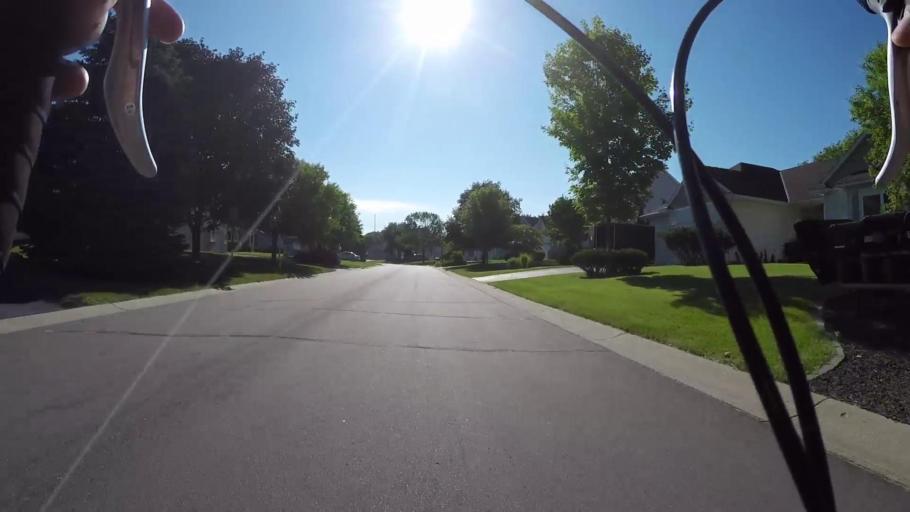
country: US
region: Minnesota
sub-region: Hennepin County
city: Eden Prairie
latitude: 44.8748
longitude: -93.4983
